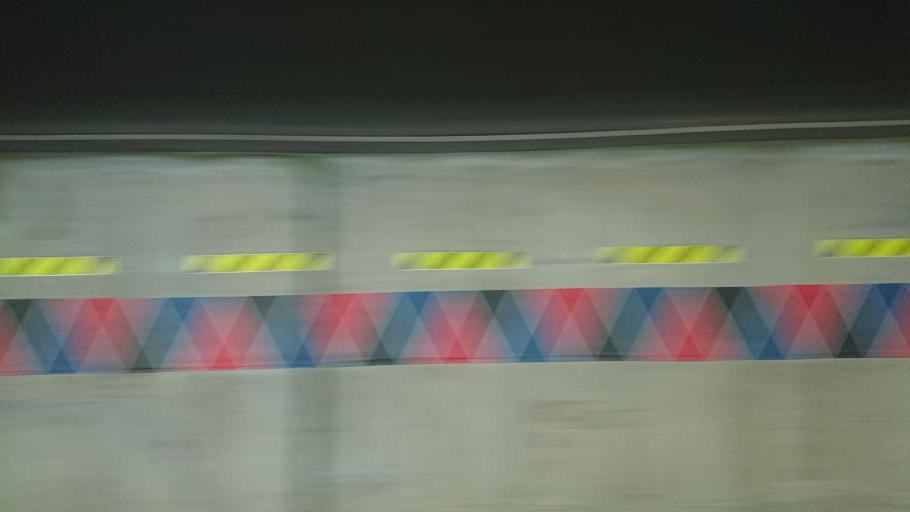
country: TW
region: Taiwan
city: Lugu
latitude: 23.4754
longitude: 120.7334
